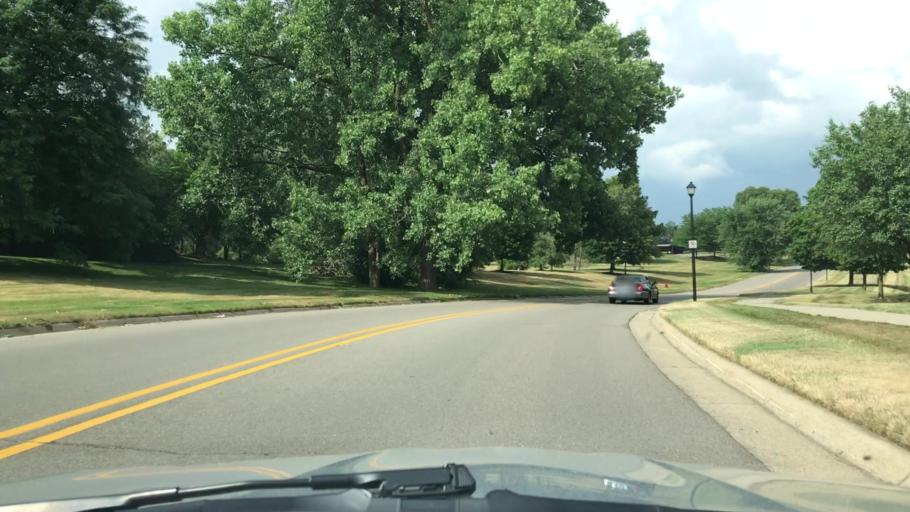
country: US
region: Michigan
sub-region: Wayne County
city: Northville
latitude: 42.4350
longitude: -83.4647
